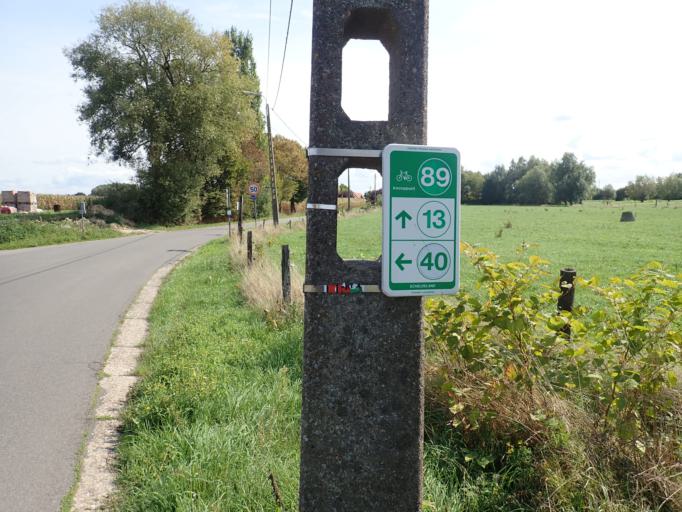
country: BE
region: Flanders
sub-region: Provincie Antwerpen
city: Bornem
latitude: 51.0796
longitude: 4.2374
